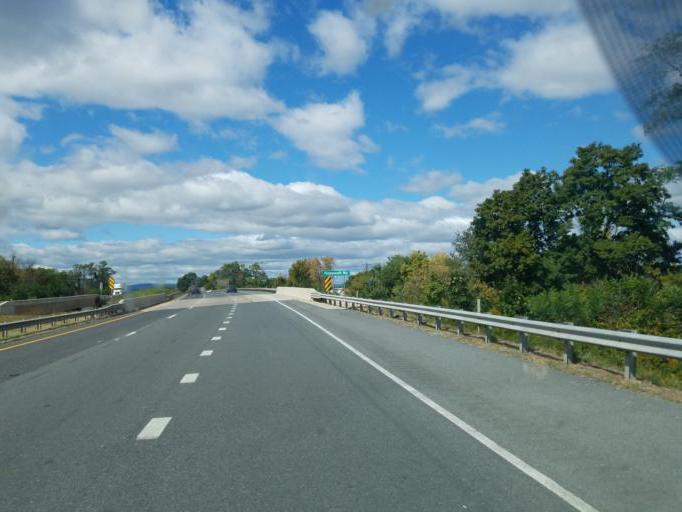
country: US
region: Maryland
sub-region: Washington County
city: Halfway
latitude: 39.6215
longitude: -77.7893
